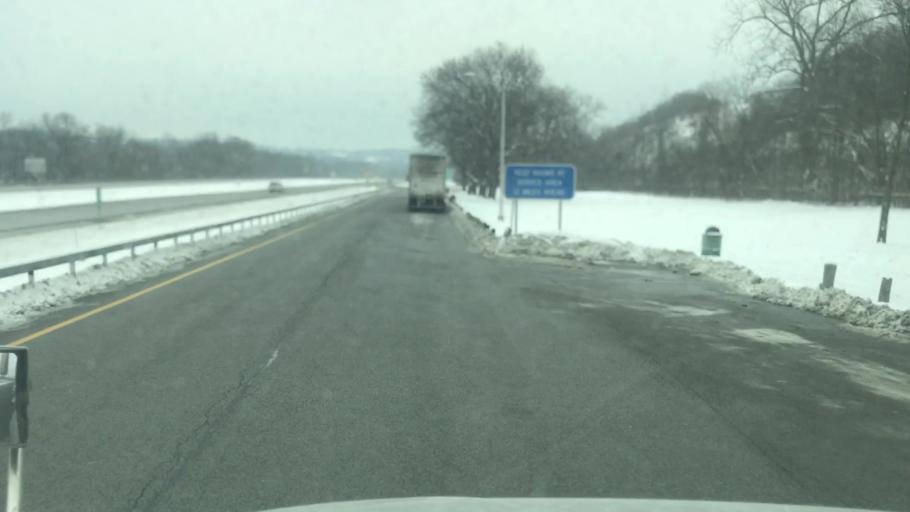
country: US
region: New York
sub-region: Montgomery County
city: Fonda
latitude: 42.9436
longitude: -74.3943
